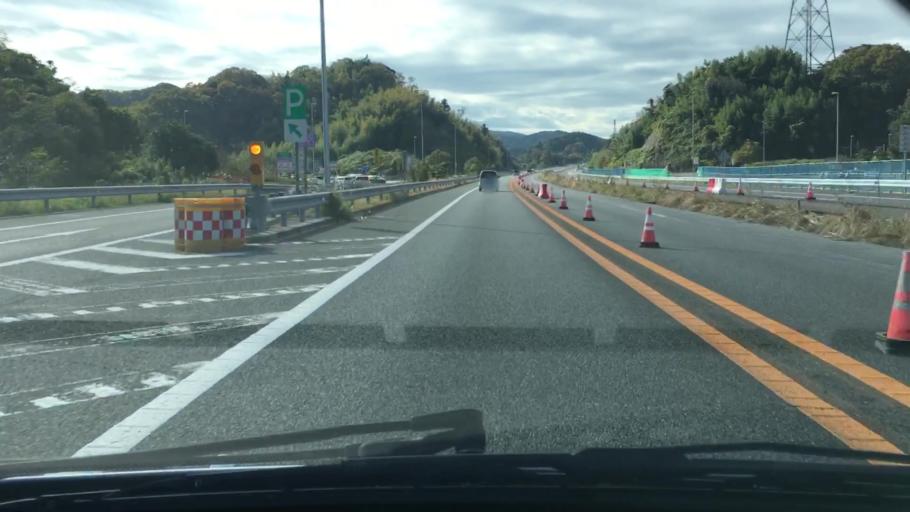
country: JP
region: Chiba
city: Kimitsu
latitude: 35.2845
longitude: 139.9272
